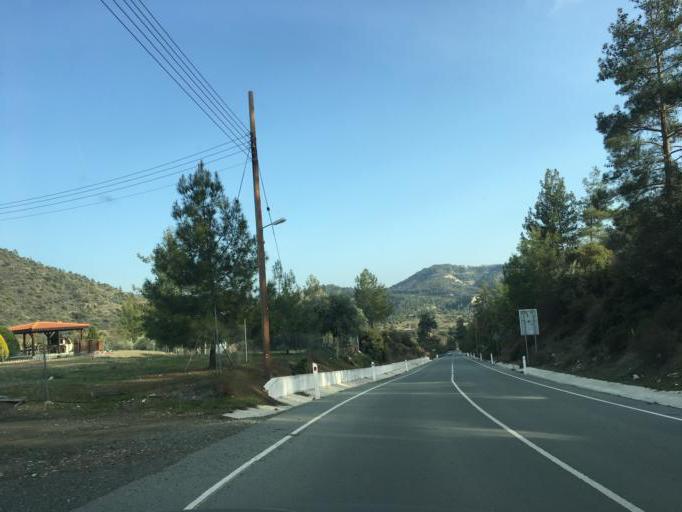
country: CY
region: Limassol
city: Pelendri
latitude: 34.8303
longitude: 32.9614
